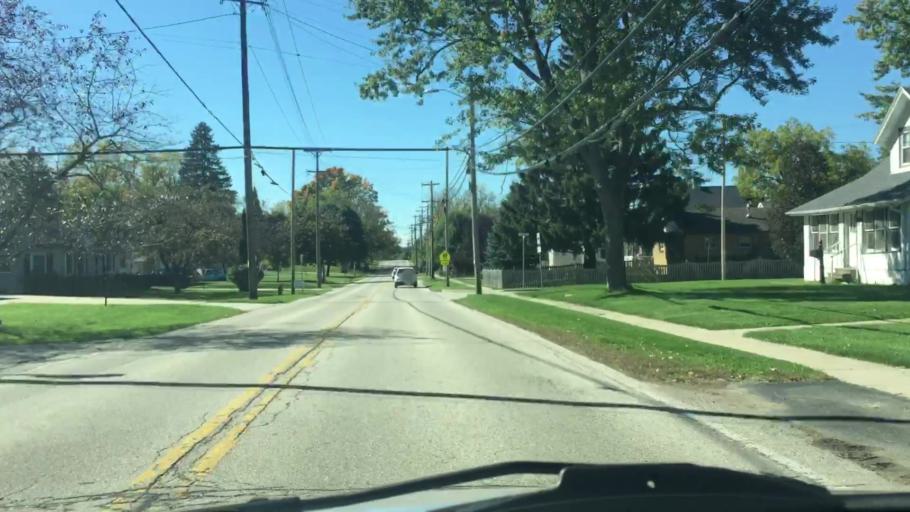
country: US
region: Wisconsin
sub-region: Waukesha County
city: Pewaukee
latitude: 43.0773
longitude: -88.2659
